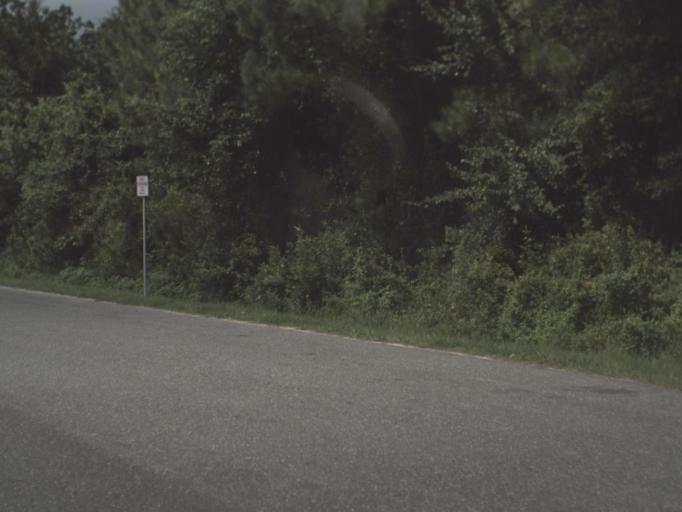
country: US
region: Florida
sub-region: Baker County
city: Macclenny
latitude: 30.3234
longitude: -82.1250
